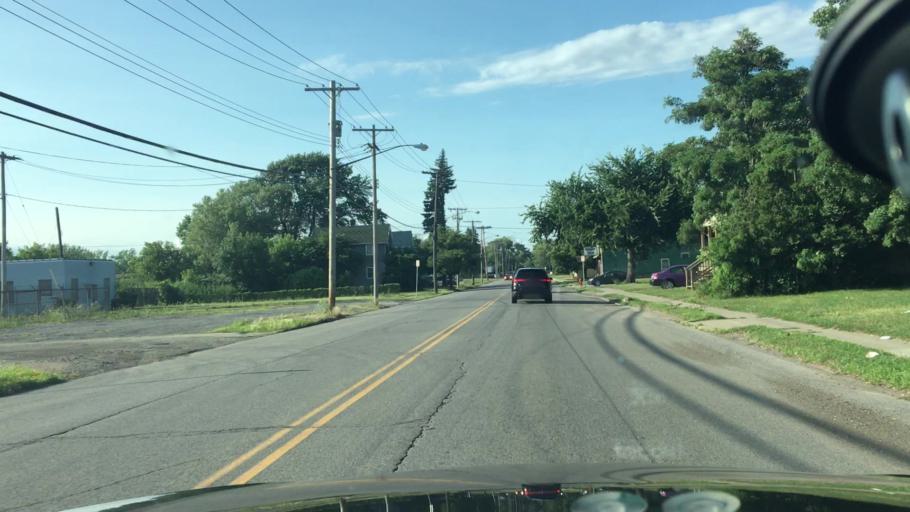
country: US
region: New York
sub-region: Erie County
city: Lackawanna
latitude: 42.8500
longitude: -78.8323
